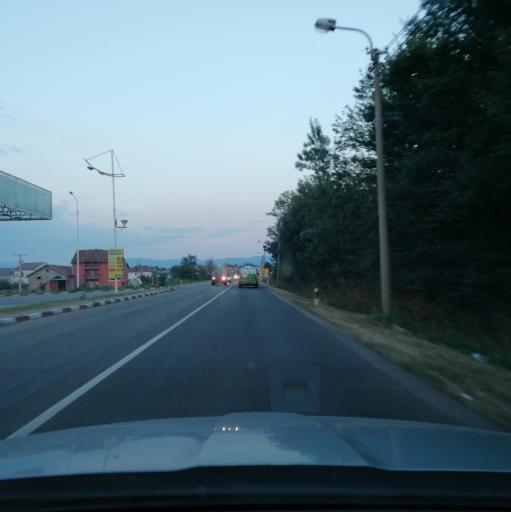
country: RS
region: Central Serbia
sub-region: Raski Okrug
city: Kraljevo
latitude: 43.7026
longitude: 20.7432
